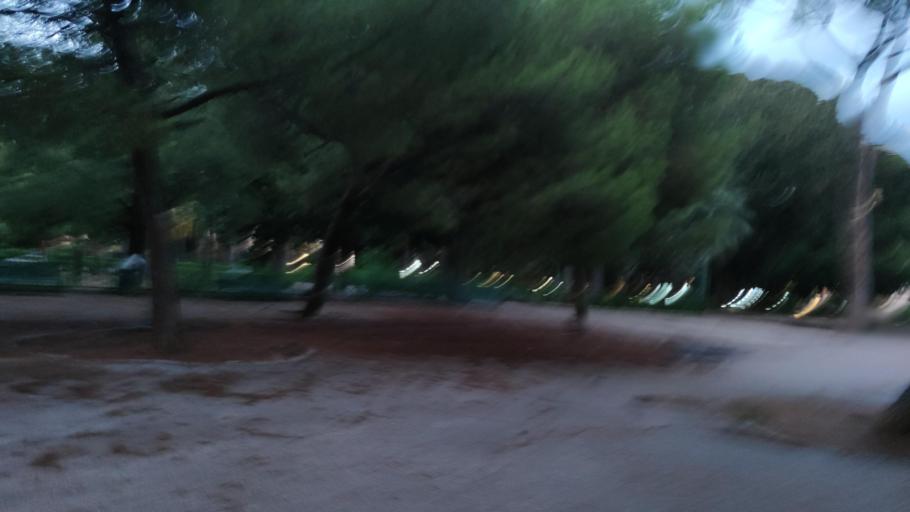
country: IT
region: Sicily
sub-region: Palermo
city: Palermo
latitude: 38.1330
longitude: 13.3518
